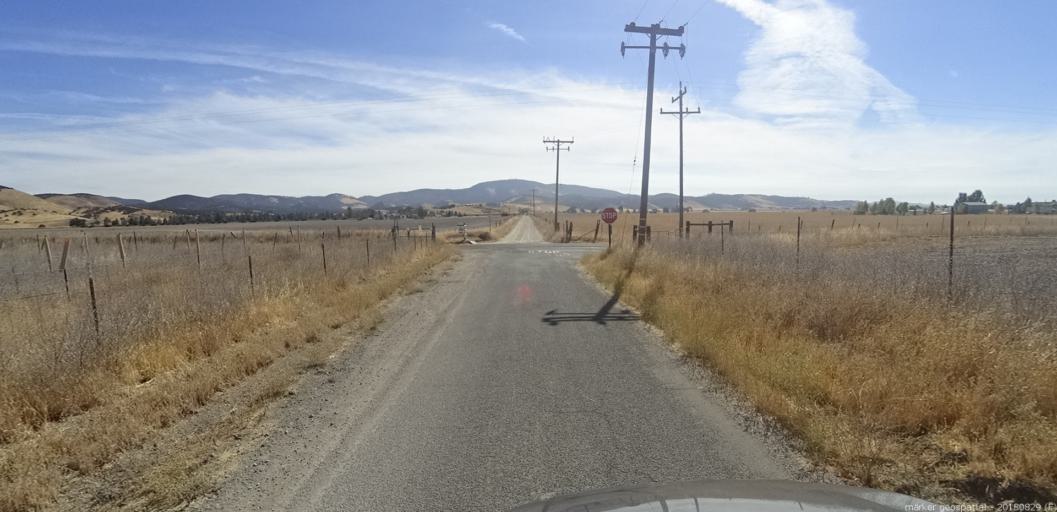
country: US
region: California
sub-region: Monterey County
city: King City
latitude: 35.9513
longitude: -121.0830
